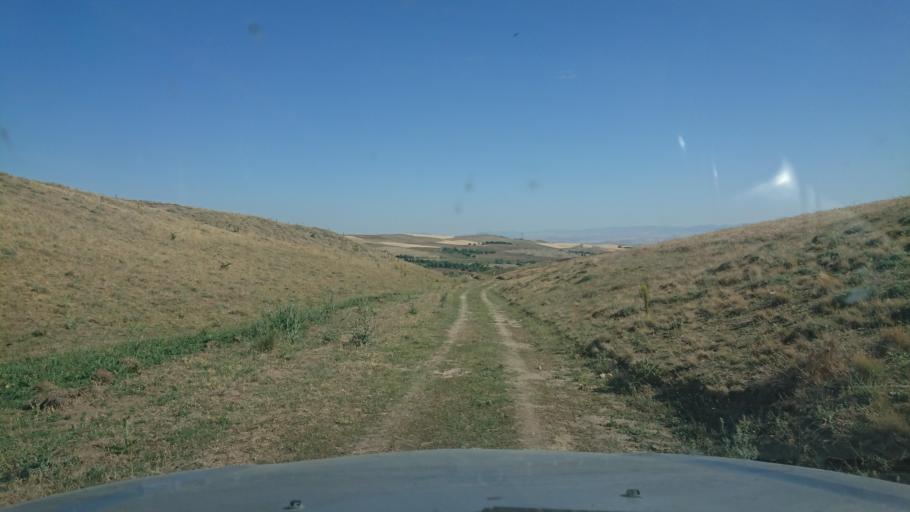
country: TR
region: Aksaray
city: Agacoren
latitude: 38.8348
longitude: 33.9274
